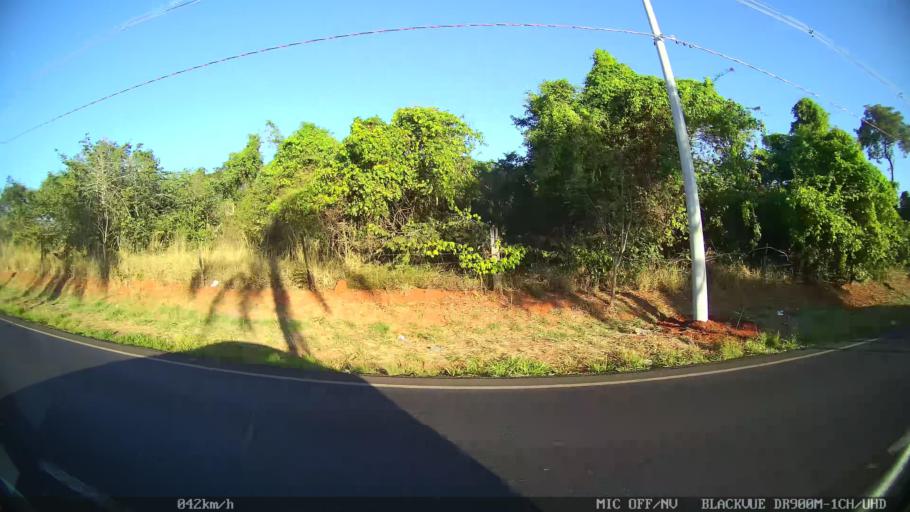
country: BR
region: Sao Paulo
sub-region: Sao Jose Do Rio Preto
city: Sao Jose do Rio Preto
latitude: -20.7670
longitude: -49.3549
